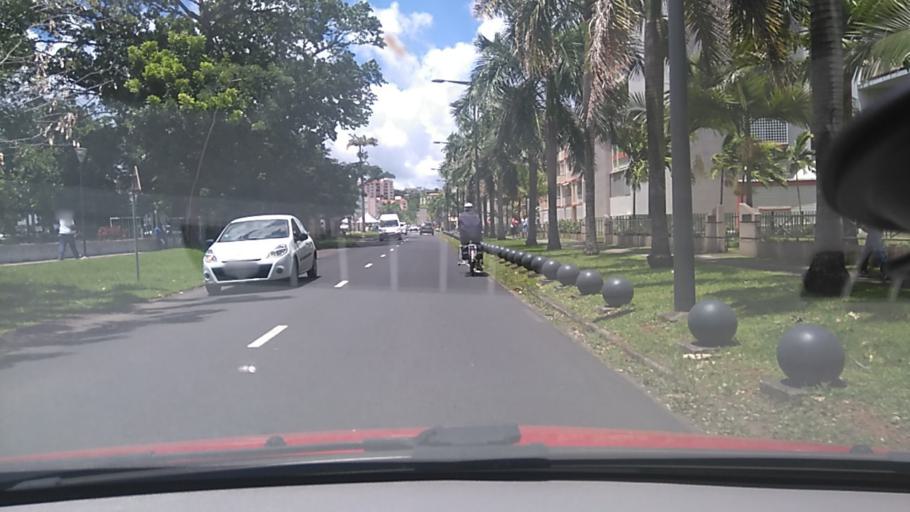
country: MQ
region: Martinique
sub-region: Martinique
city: Fort-de-France
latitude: 14.6103
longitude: -61.0495
